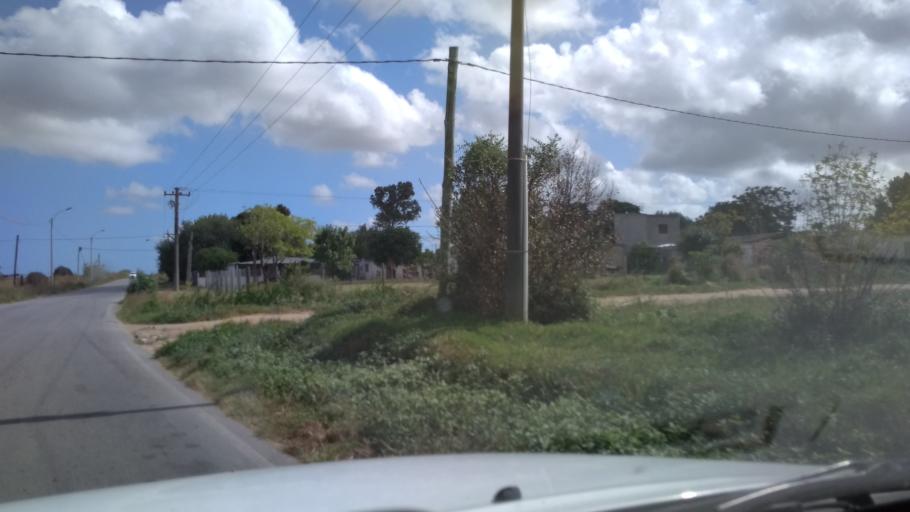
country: UY
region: Canelones
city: Colonia Nicolich
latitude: -34.7789
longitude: -56.0185
